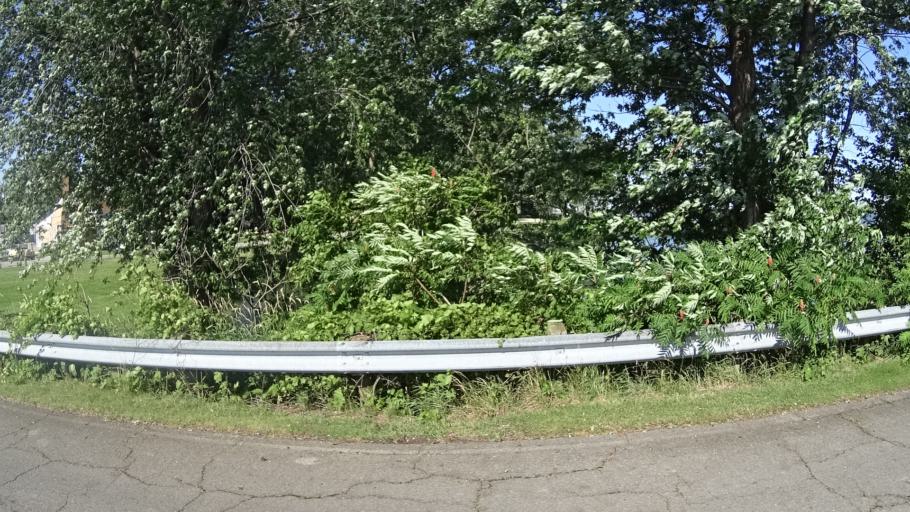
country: US
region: Ohio
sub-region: Ottawa County
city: Port Clinton
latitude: 41.4736
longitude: -82.8260
